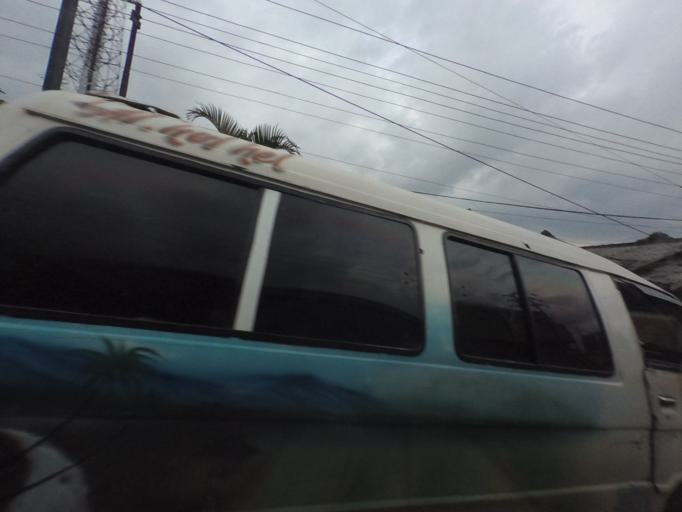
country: ID
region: West Java
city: Cicurug
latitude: -6.8367
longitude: 106.7604
